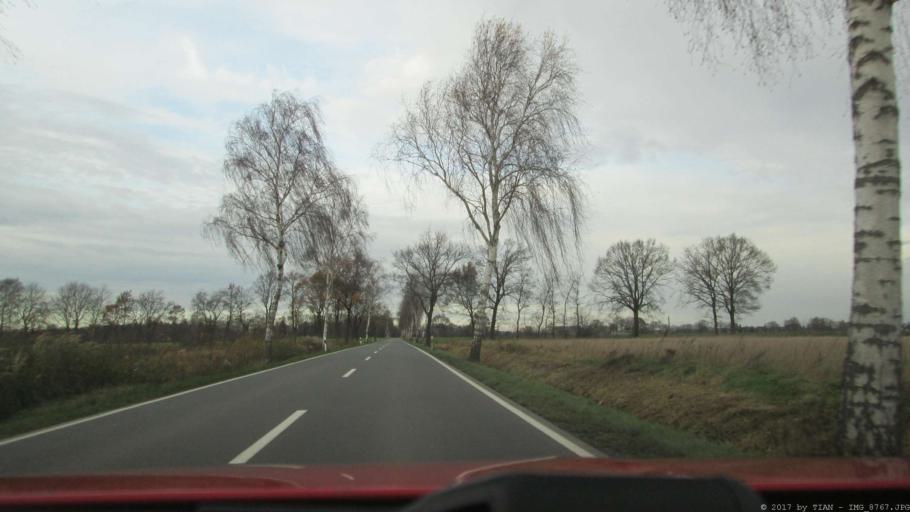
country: DE
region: Lower Saxony
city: Tiddische
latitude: 52.4893
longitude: 10.8079
